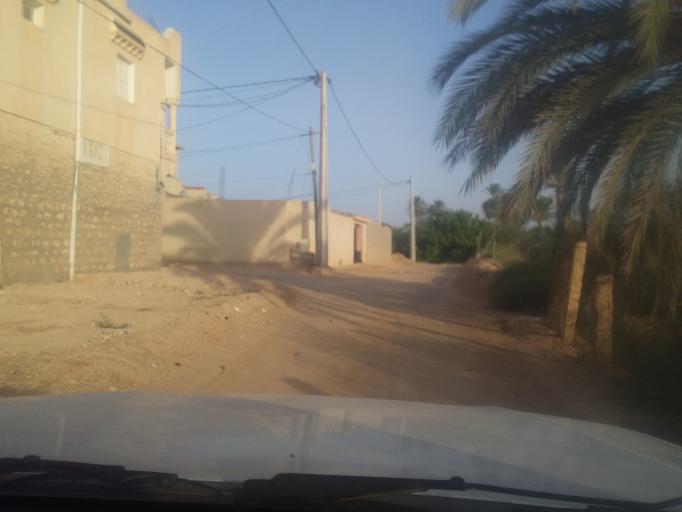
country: TN
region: Qabis
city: Gabes
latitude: 33.6289
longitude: 10.2894
